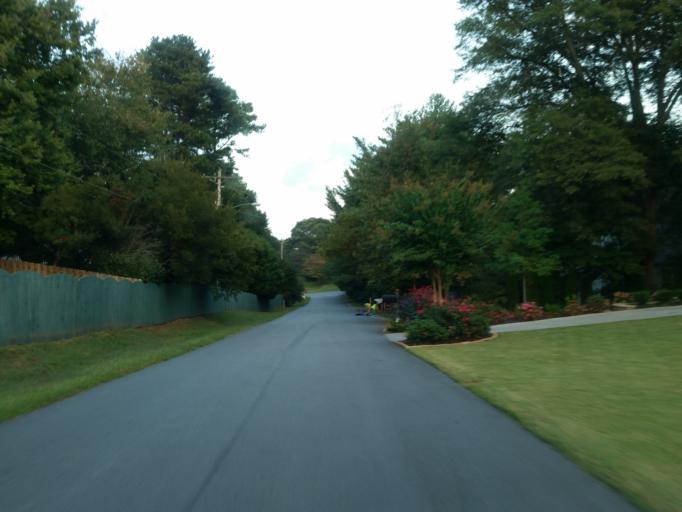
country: US
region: Georgia
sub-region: Cobb County
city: Marietta
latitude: 33.9978
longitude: -84.4733
